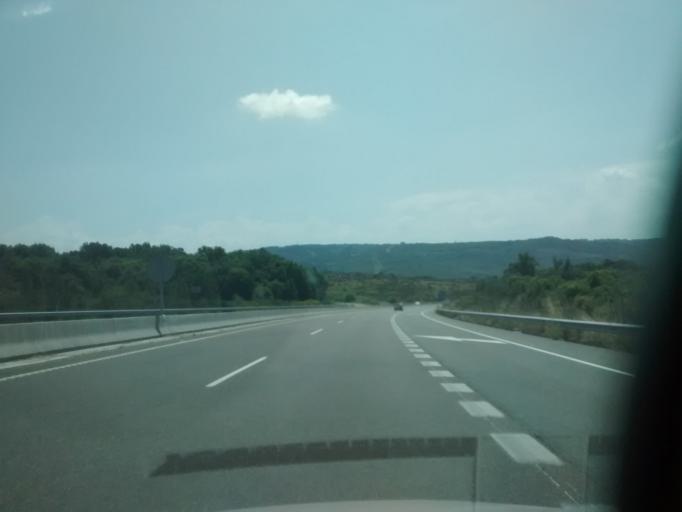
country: ES
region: Galicia
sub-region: Provincia de Ourense
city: Maside
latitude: 42.3987
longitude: -8.0024
